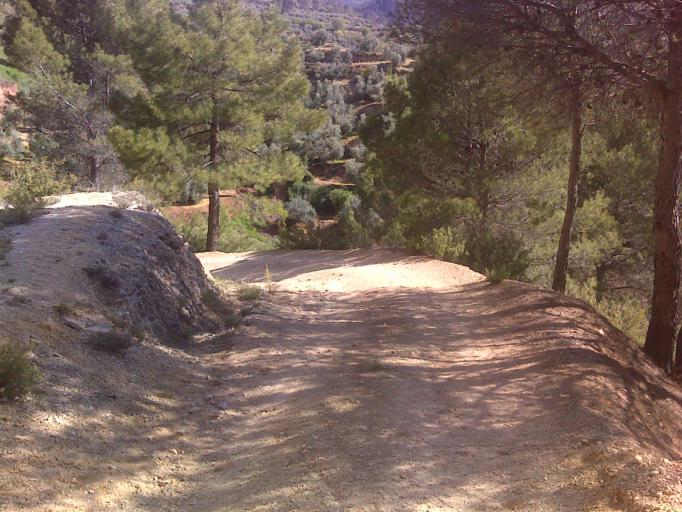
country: ES
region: Andalusia
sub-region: Provincia de Jaen
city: Siles
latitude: 38.3739
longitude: -2.5756
